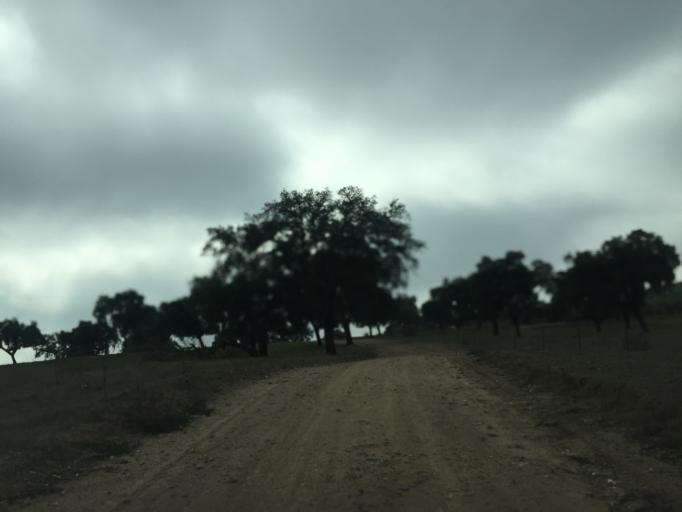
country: PT
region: Portalegre
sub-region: Fronteira
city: Fronteira
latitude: 39.0654
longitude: -7.6281
